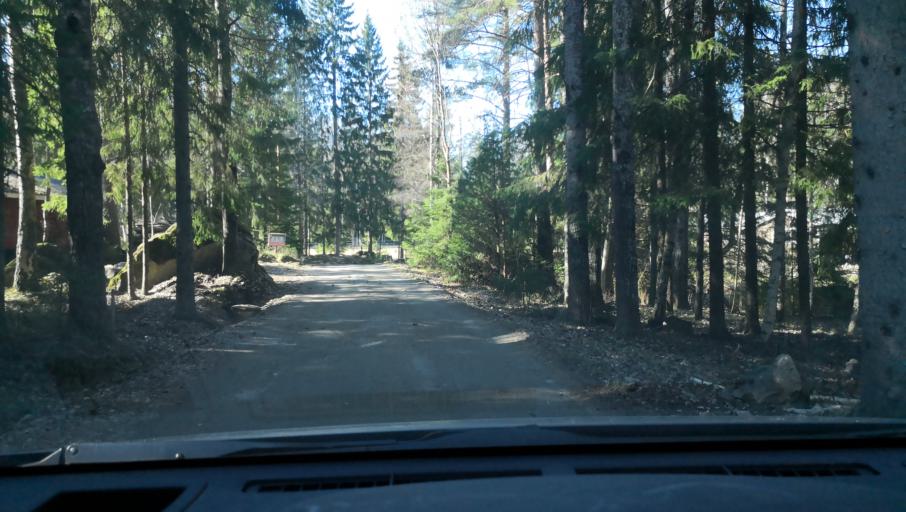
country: SE
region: Vaestmanland
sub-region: Sala Kommun
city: Sala
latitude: 59.9431
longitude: 16.4395
